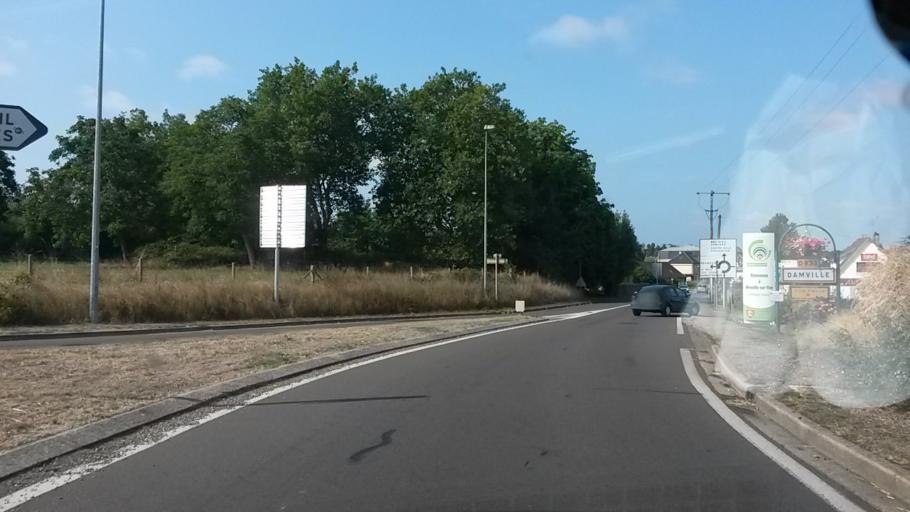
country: FR
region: Haute-Normandie
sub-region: Departement de l'Eure
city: Damville
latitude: 48.8719
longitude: 1.0816
